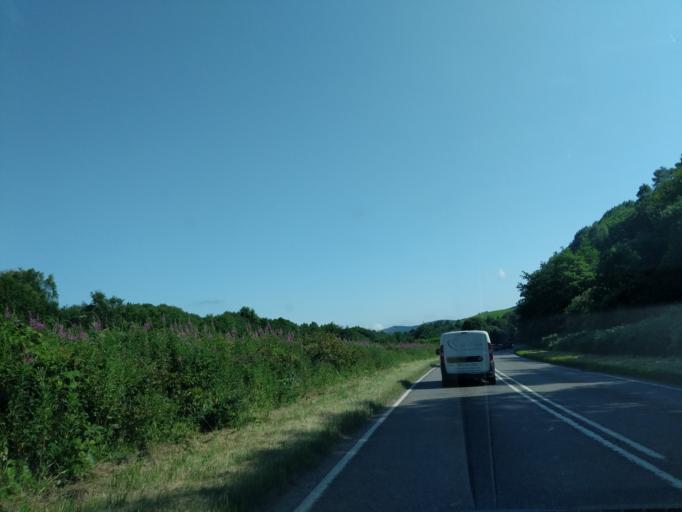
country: GB
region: Scotland
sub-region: Moray
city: Rothes
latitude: 57.5136
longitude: -3.2056
